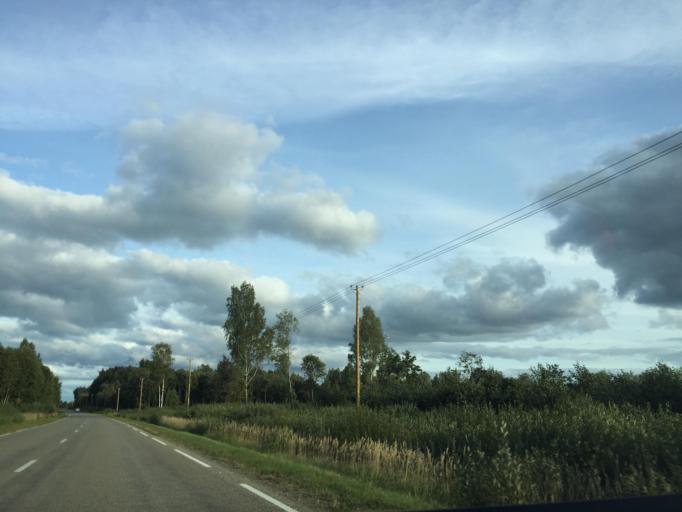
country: LV
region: Nereta
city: Nereta
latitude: 56.2895
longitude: 25.1257
